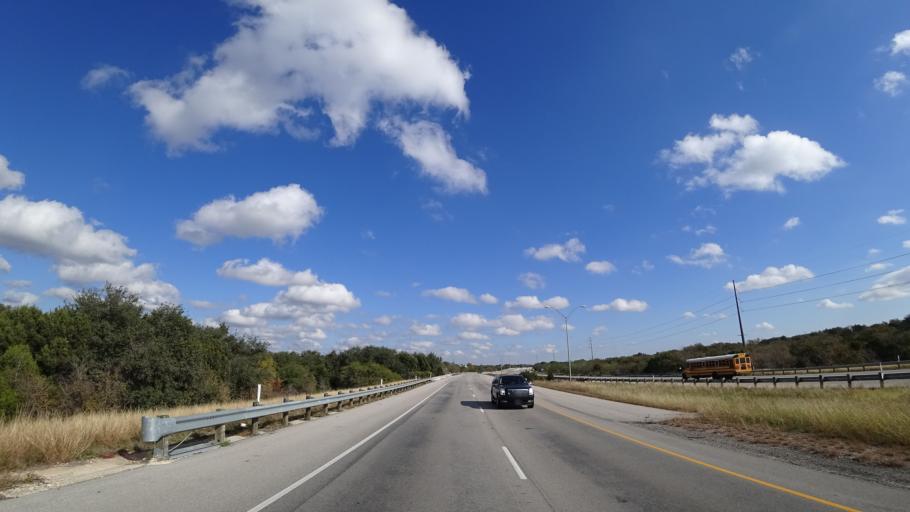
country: US
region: Texas
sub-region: Travis County
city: Shady Hollow
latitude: 30.2116
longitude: -97.8582
